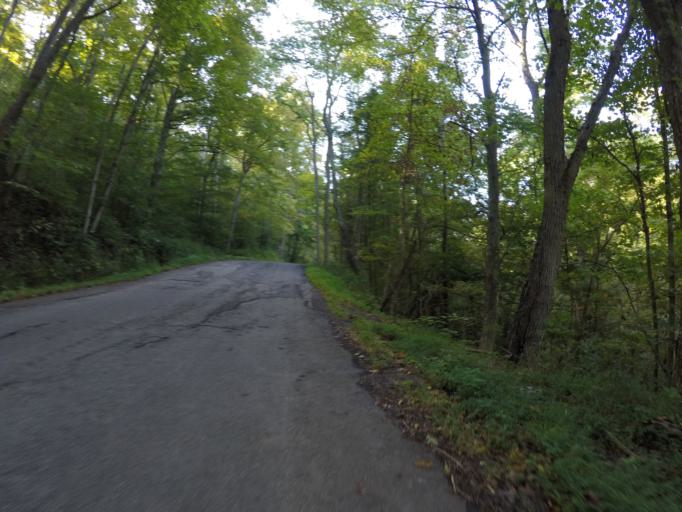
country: US
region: Kentucky
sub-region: Boyd County
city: Ashland
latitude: 38.5285
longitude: -82.5334
